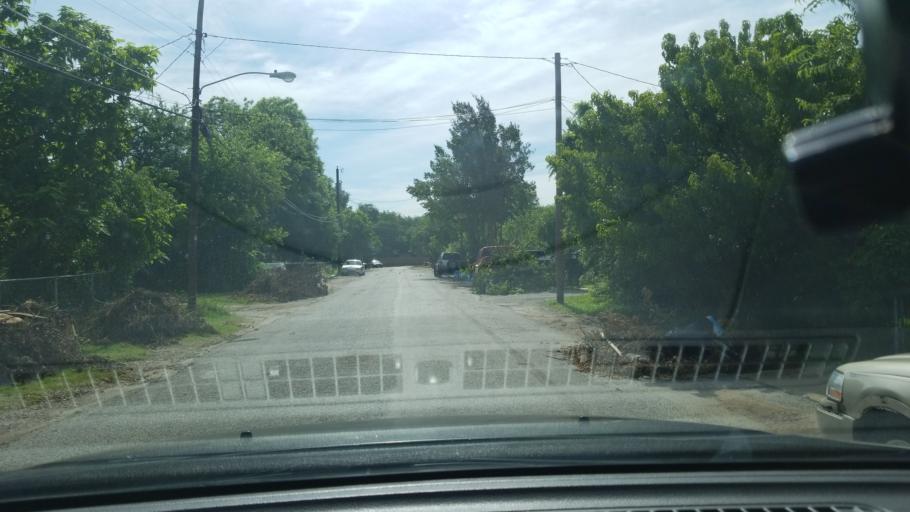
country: US
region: Texas
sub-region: Dallas County
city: Balch Springs
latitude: 32.7674
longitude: -96.6798
